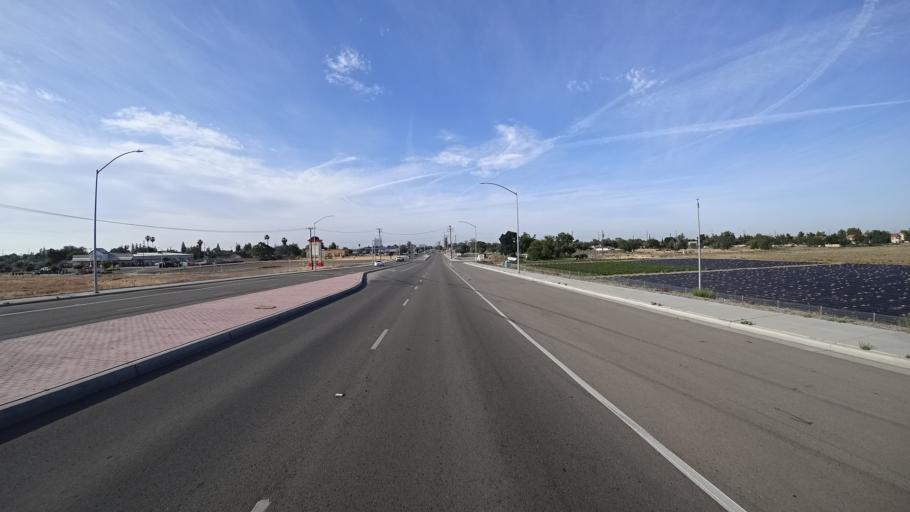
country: US
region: California
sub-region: Kings County
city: Hanford
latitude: 36.3167
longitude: -119.6731
